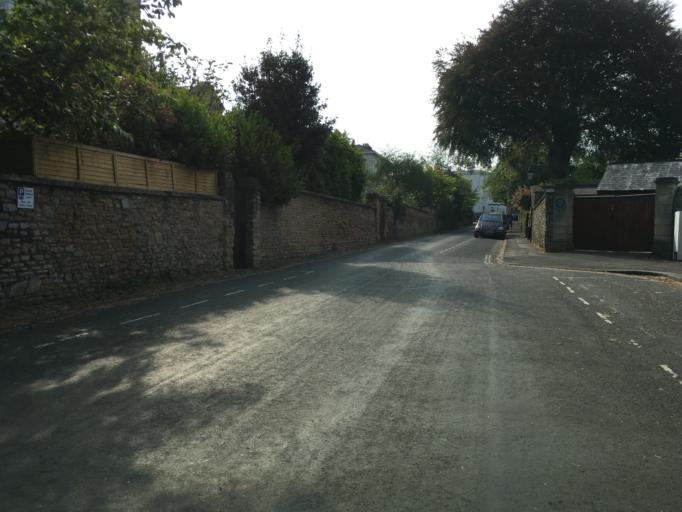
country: GB
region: England
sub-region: Bristol
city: Bristol
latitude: 51.4594
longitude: -2.6234
